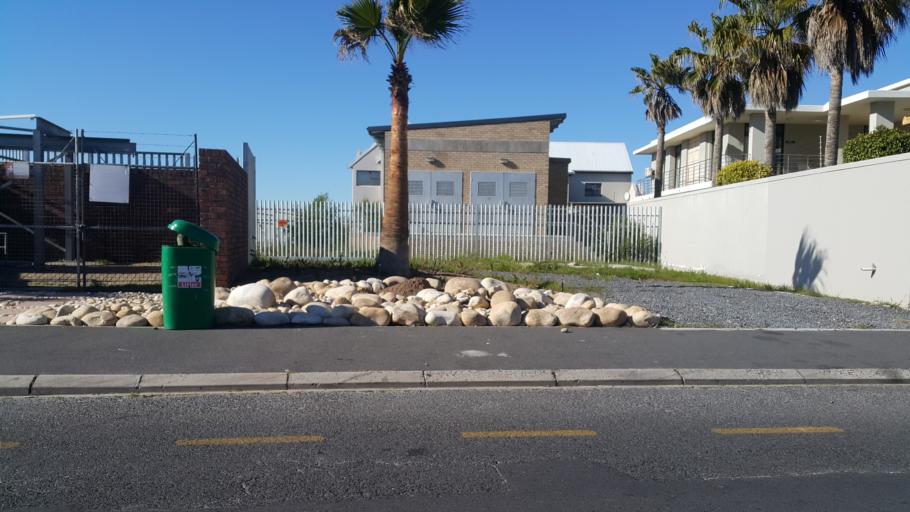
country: ZA
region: Western Cape
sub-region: City of Cape Town
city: Sunset Beach
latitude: -33.8551
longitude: 18.4961
